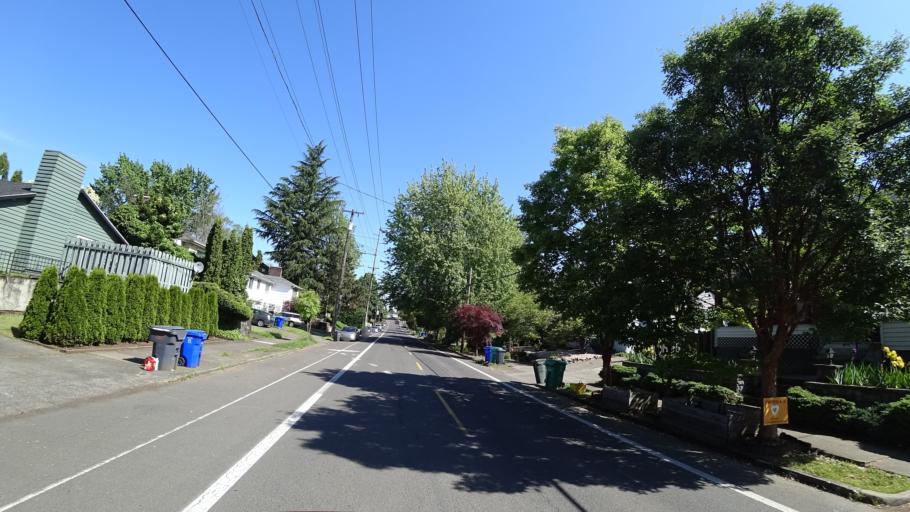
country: US
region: Oregon
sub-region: Clackamas County
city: Milwaukie
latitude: 45.4954
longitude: -122.6189
